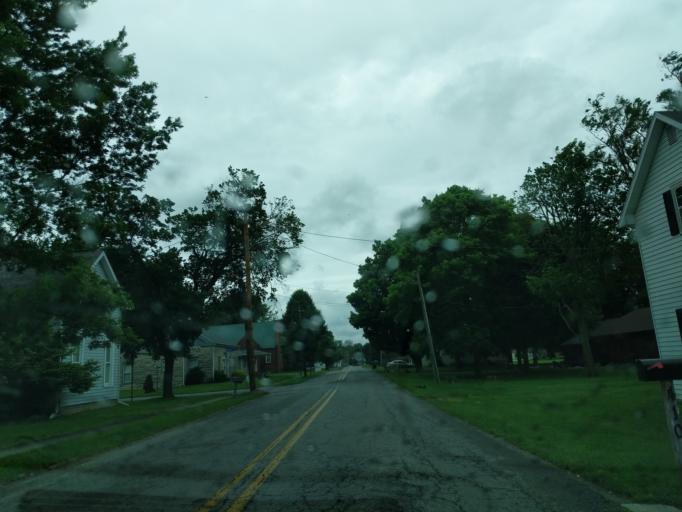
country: US
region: Indiana
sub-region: Madison County
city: Chesterfield
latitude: 40.1096
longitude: -85.5958
